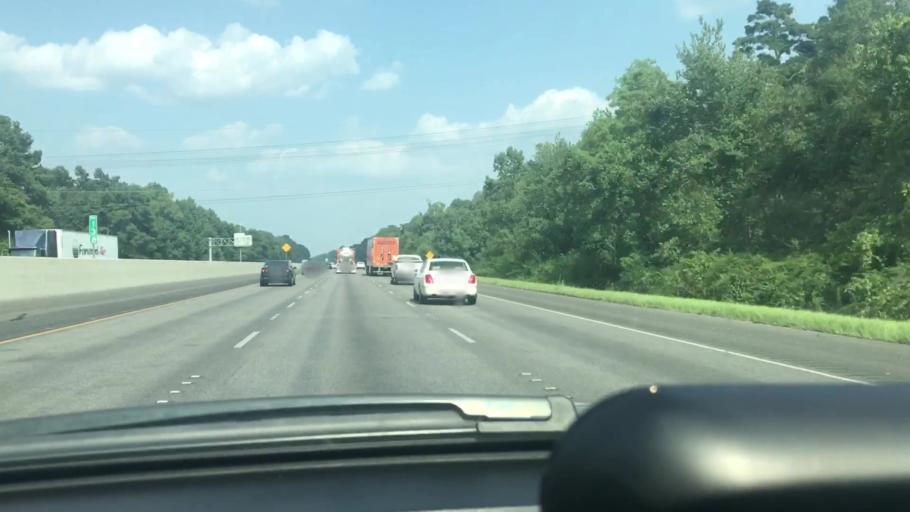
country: US
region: Louisiana
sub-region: Livingston Parish
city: Walker
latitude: 30.4660
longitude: -90.8986
